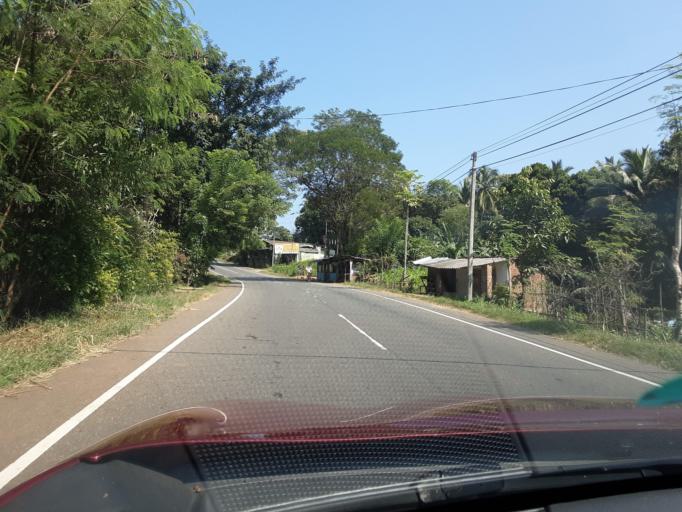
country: LK
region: Uva
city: Badulla
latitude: 7.1726
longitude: 81.0503
